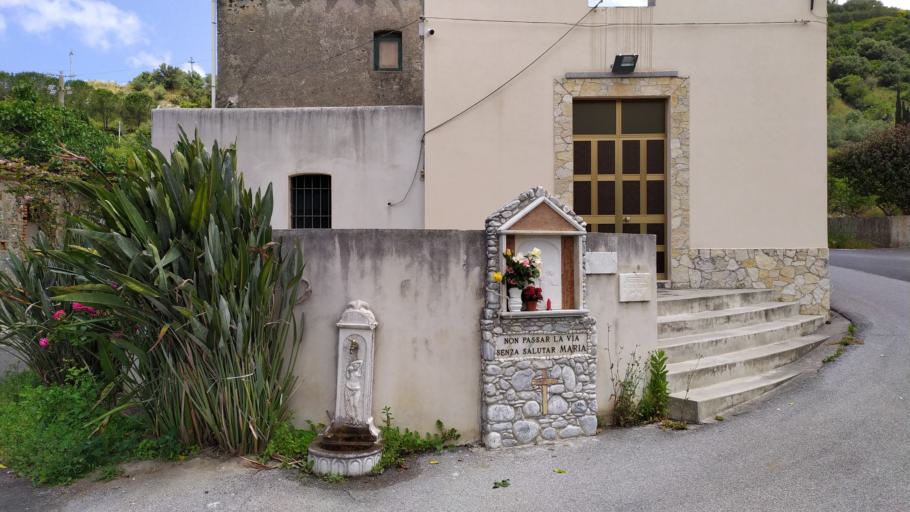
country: IT
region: Sicily
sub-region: Messina
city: San Pier Niceto
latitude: 38.1674
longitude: 15.3642
